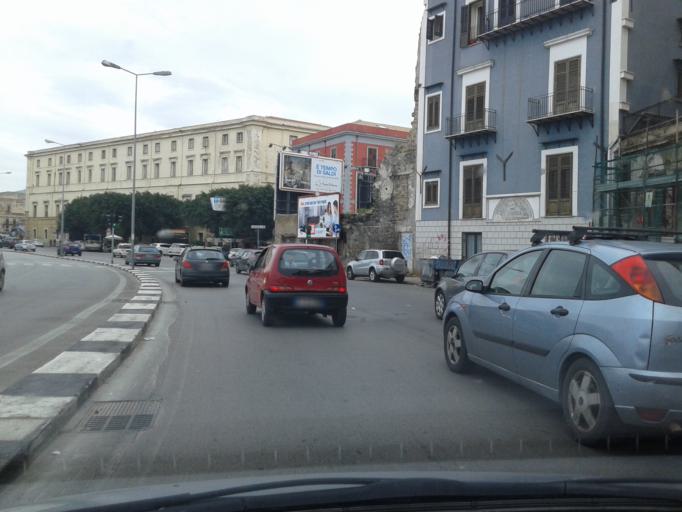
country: IT
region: Sicily
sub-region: Palermo
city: Palermo
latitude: 38.1196
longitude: 13.3666
